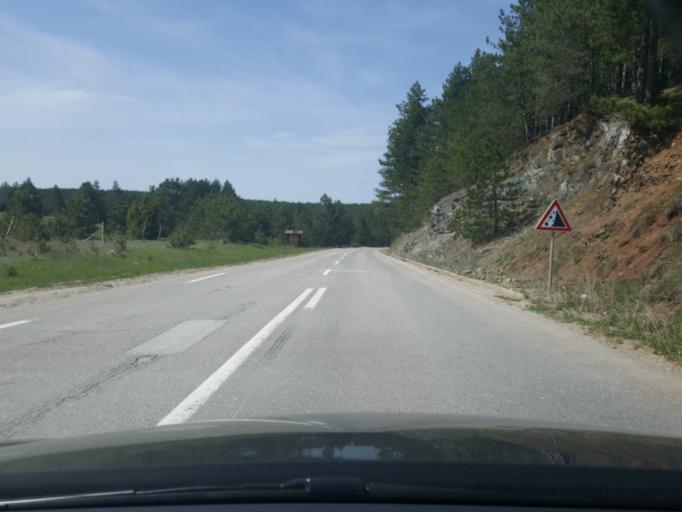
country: RS
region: Central Serbia
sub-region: Zlatiborski Okrug
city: Cajetina
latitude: 43.8286
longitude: 19.6404
